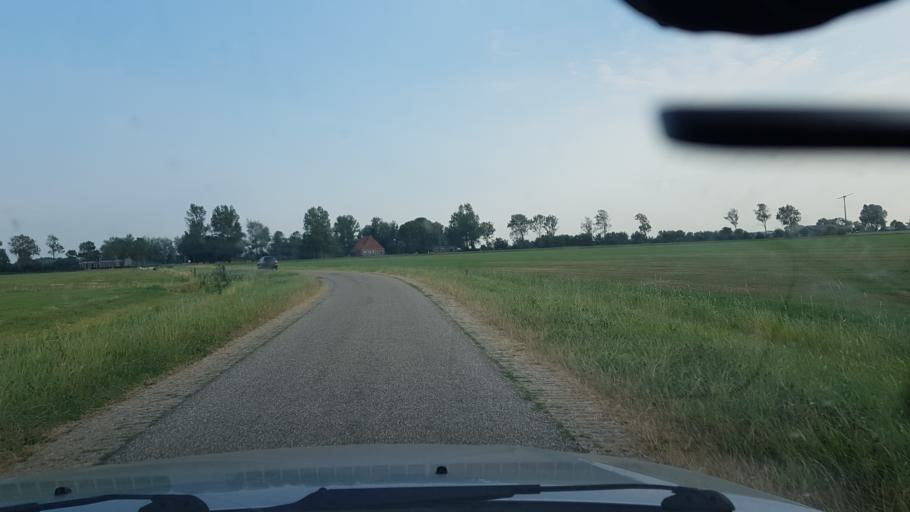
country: NL
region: Friesland
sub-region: Gemeente Ferwerderadiel
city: Burdaard
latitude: 53.3337
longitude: 5.8692
